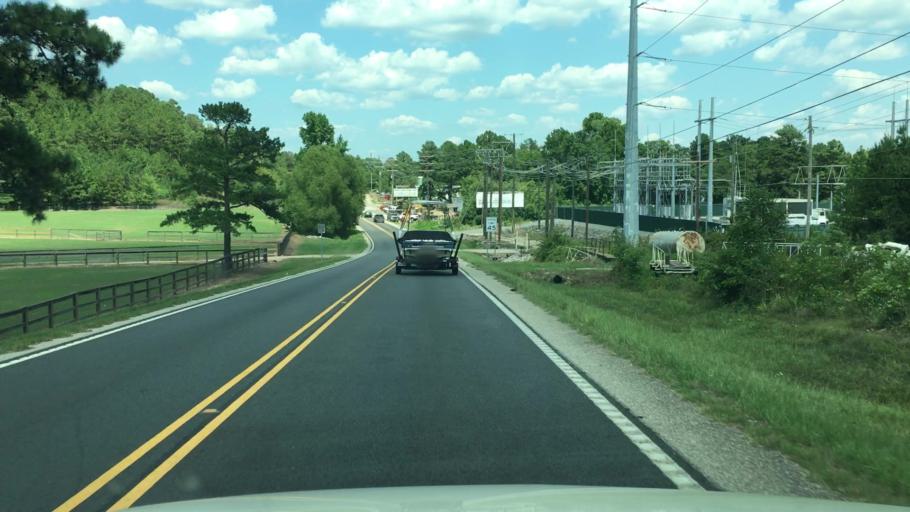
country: US
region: Arkansas
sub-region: Garland County
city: Lake Hamilton
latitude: 34.4028
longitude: -93.0940
